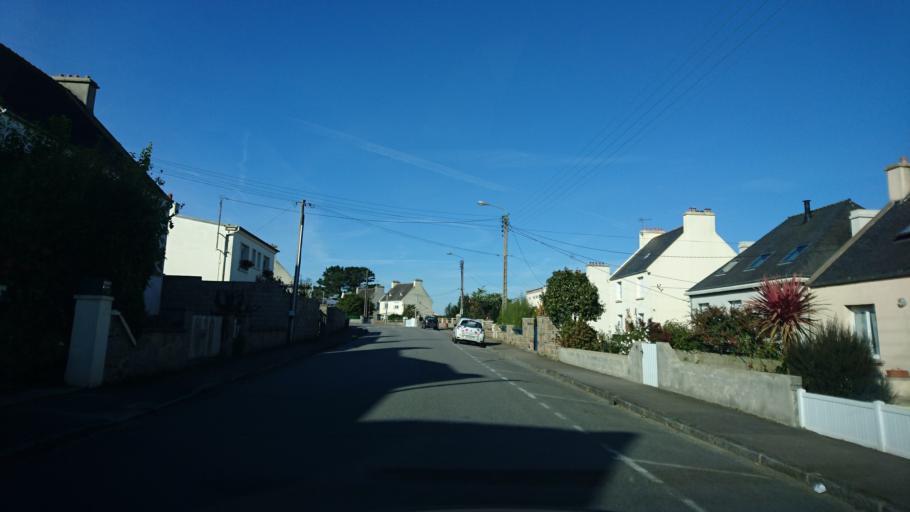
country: FR
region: Brittany
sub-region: Departement du Finistere
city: Saint-Renan
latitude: 48.4326
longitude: -4.6277
